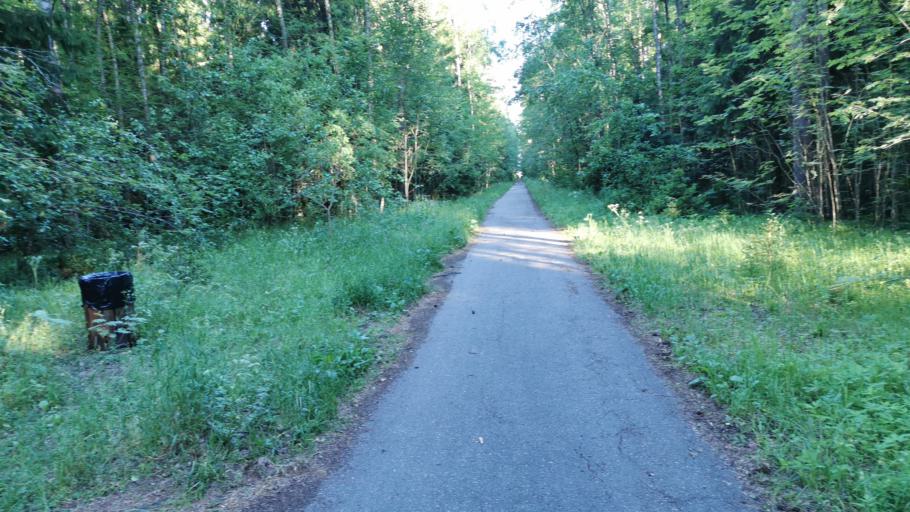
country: RU
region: St.-Petersburg
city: Ol'gino
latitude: 59.9980
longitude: 30.0779
